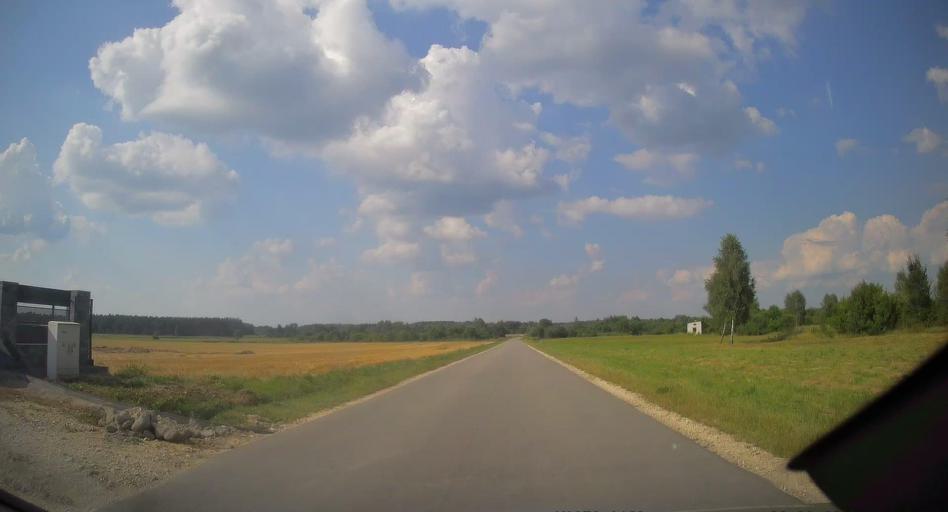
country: PL
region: Swietokrzyskie
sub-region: Powiat konecki
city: Radoszyce
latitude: 51.0854
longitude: 20.2583
